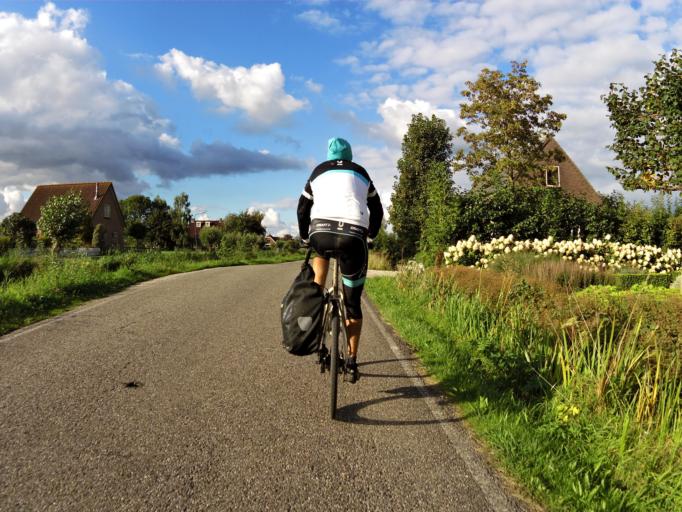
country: NL
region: Utrecht
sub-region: Gemeente Woerden
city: Woerden
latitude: 52.1348
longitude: 4.8935
